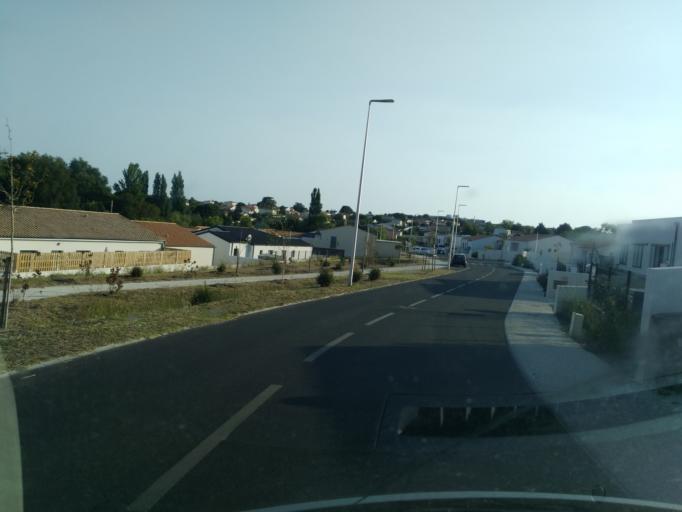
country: FR
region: Poitou-Charentes
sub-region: Departement de la Charente-Maritime
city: Vaux-sur-Mer
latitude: 45.6391
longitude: -1.0545
